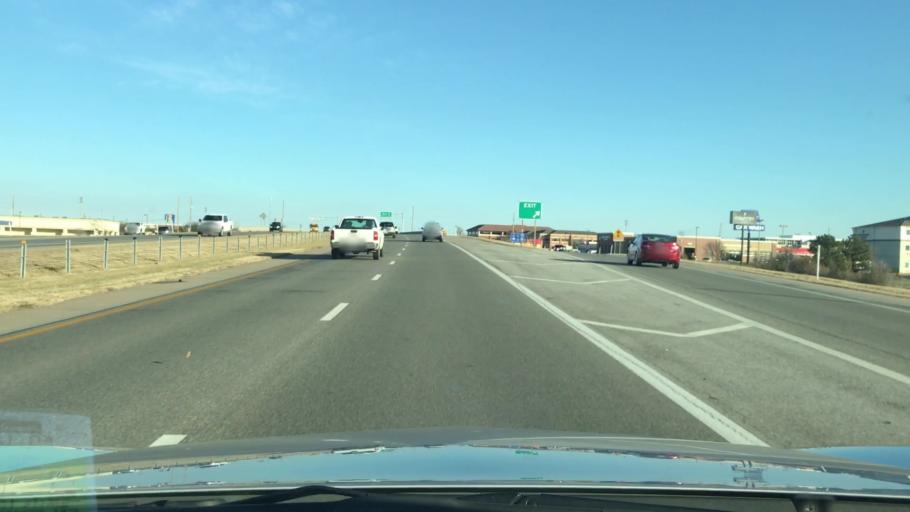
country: US
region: Kansas
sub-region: Sedgwick County
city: Bellaire
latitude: 37.7447
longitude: -97.2483
